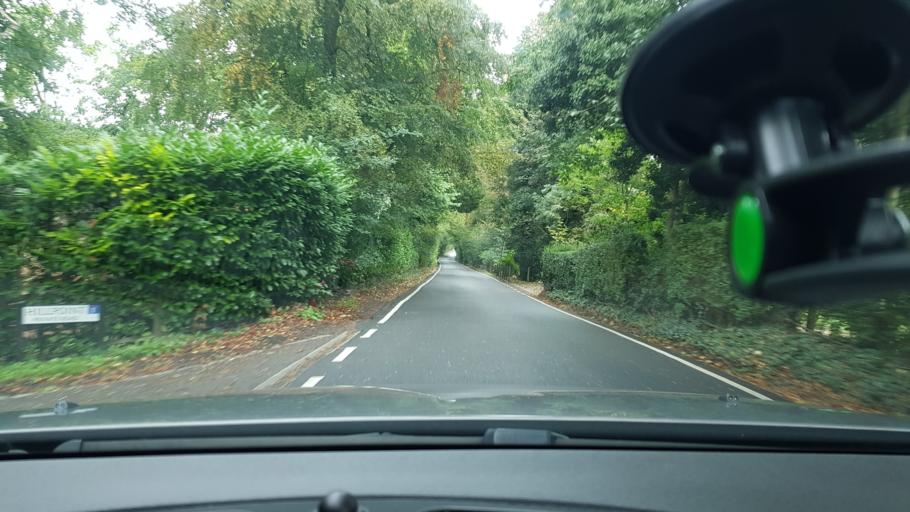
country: GB
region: England
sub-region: Hertfordshire
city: Chorleywood
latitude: 51.6511
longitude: -0.4799
